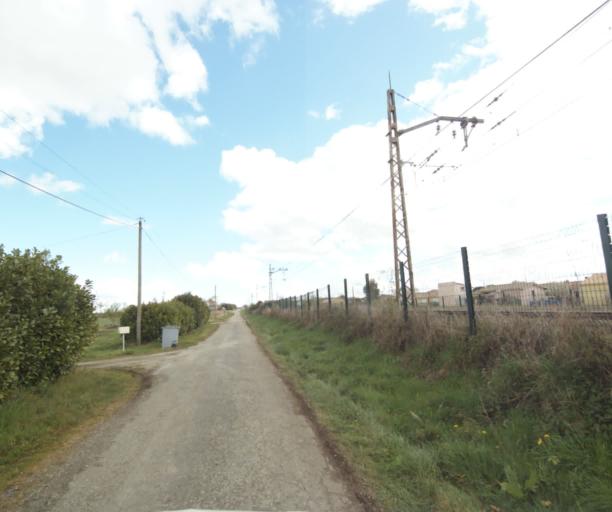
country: FR
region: Midi-Pyrenees
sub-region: Departement de l'Ariege
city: Saverdun
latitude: 43.2372
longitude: 1.5796
